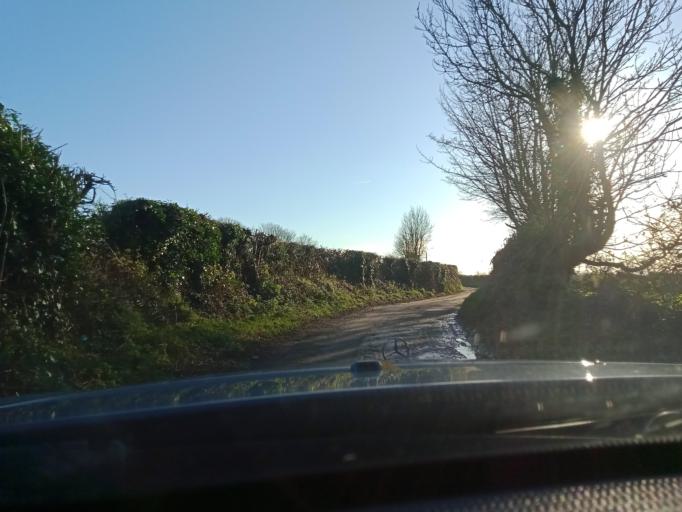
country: IE
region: Leinster
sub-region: Kilkenny
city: Mooncoin
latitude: 52.3008
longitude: -7.1943
